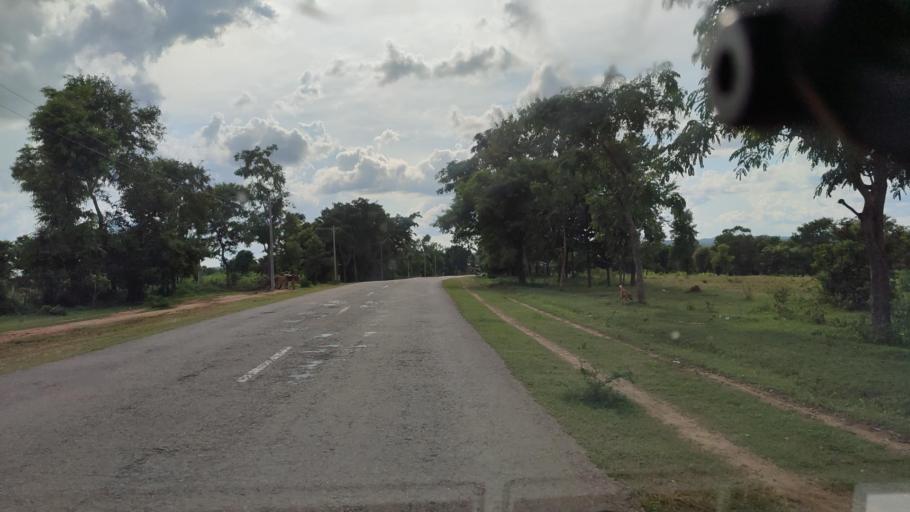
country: MM
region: Mandalay
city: Meiktila
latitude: 20.7904
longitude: 95.5230
